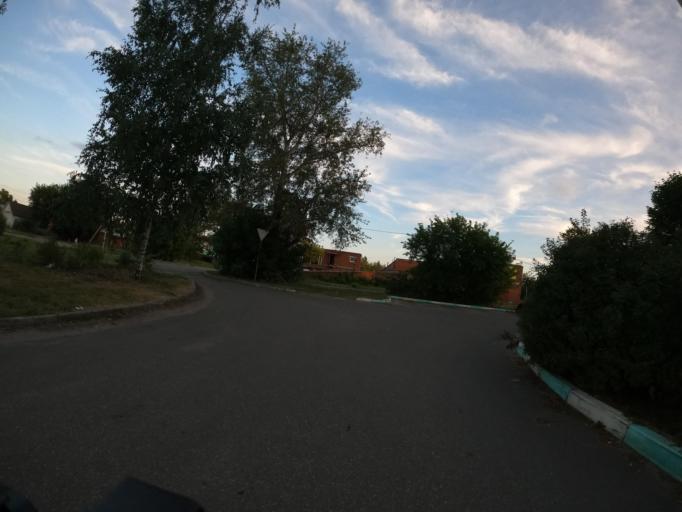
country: RU
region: Moskovskaya
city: Kolomna
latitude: 55.0979
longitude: 38.7802
